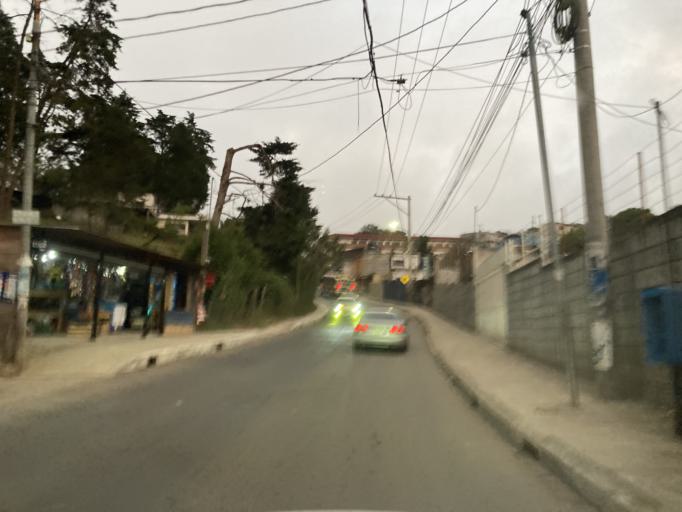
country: GT
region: Guatemala
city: San Jose Pinula
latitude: 14.5620
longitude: -90.4376
